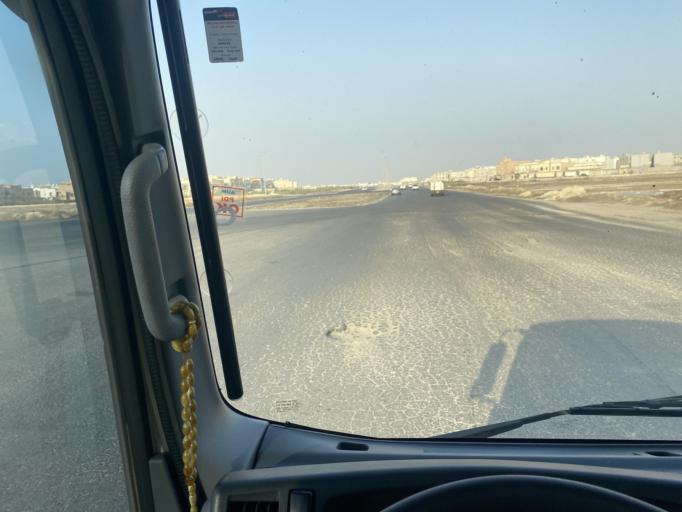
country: SA
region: Eastern Province
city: Sayhat
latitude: 26.4026
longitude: 49.9954
